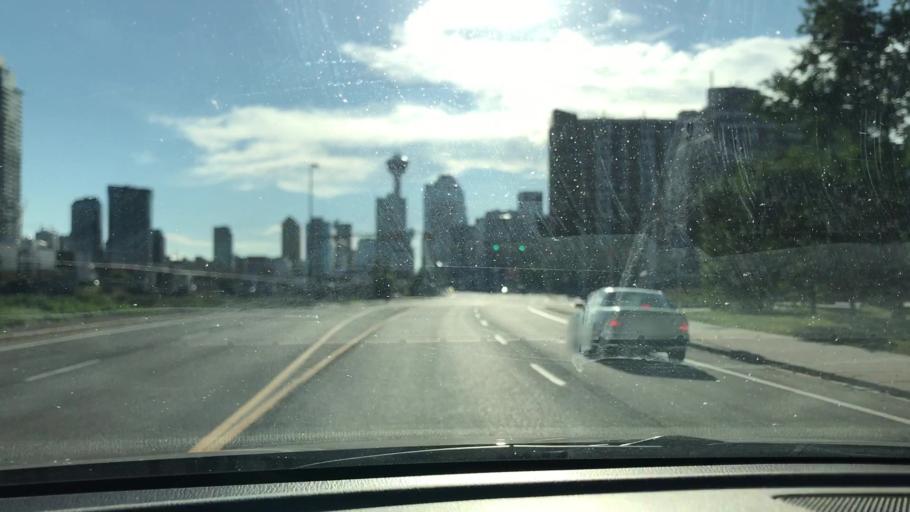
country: CA
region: Alberta
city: Calgary
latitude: 51.0440
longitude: -114.0472
